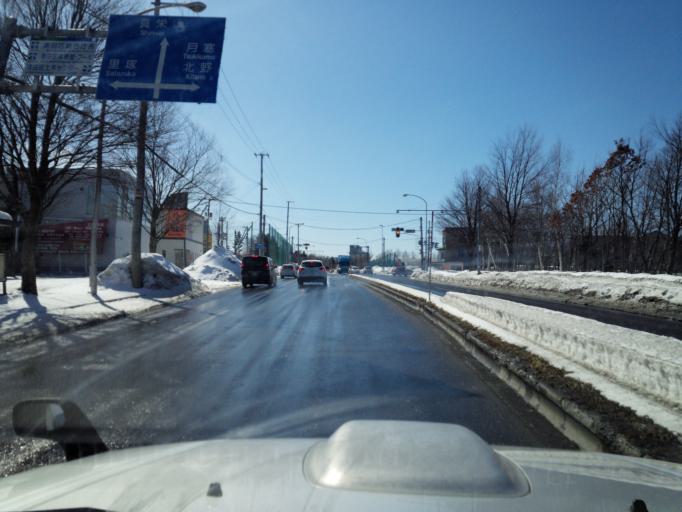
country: JP
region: Hokkaido
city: Kitahiroshima
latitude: 42.9949
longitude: 141.4579
